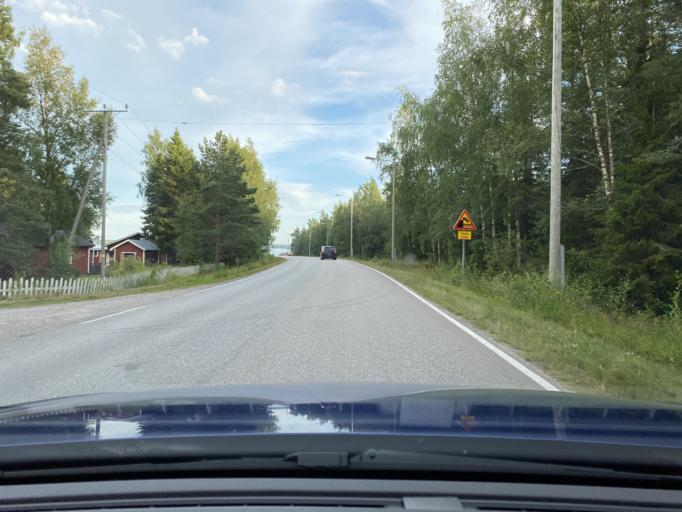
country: FI
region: Ostrobothnia
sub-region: Vaasa
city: Korsnaes
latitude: 62.9462
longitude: 21.1756
